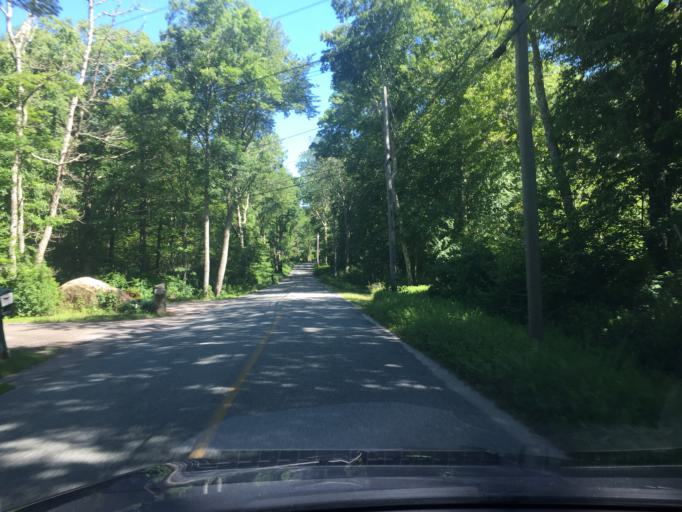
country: US
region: Rhode Island
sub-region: Washington County
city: Hopkinton
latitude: 41.4837
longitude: -71.8100
